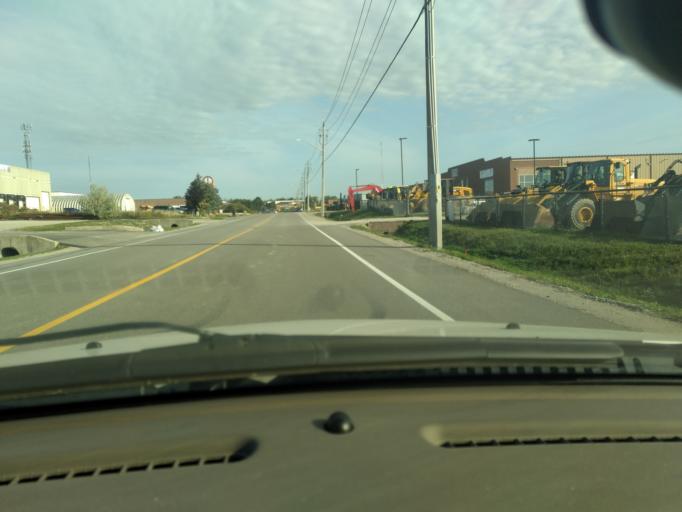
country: CA
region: Ontario
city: Innisfil
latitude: 44.3276
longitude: -79.6801
